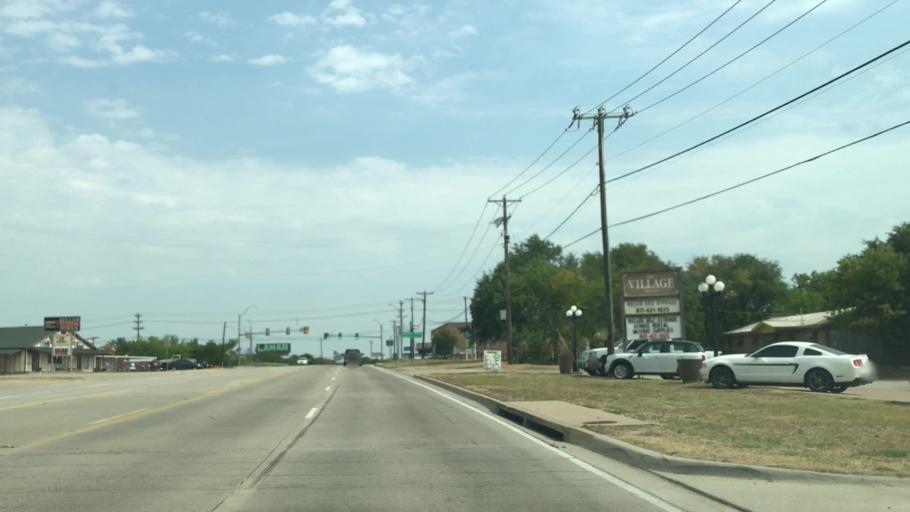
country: US
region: Texas
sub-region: Tarrant County
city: Keller
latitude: 32.9402
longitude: -97.2534
